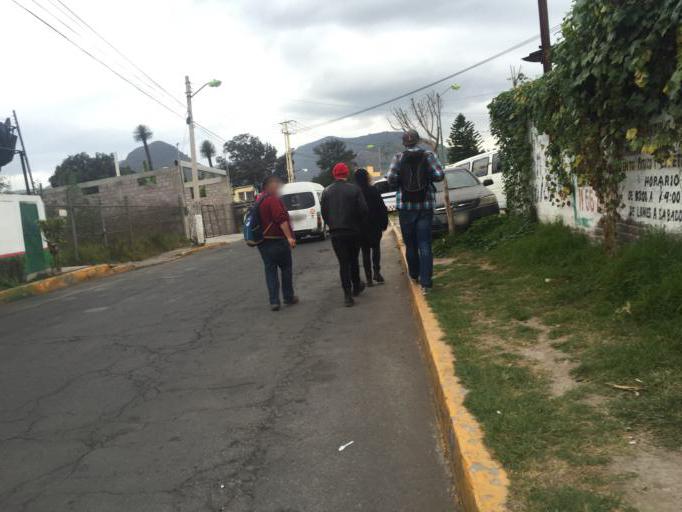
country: MX
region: Mexico
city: Ecatepec
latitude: 19.6015
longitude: -99.0421
